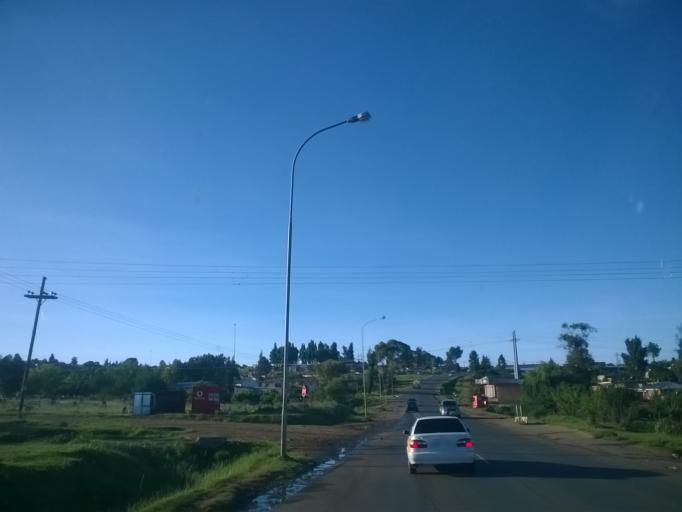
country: LS
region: Maseru
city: Maseru
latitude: -29.2804
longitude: 27.5285
